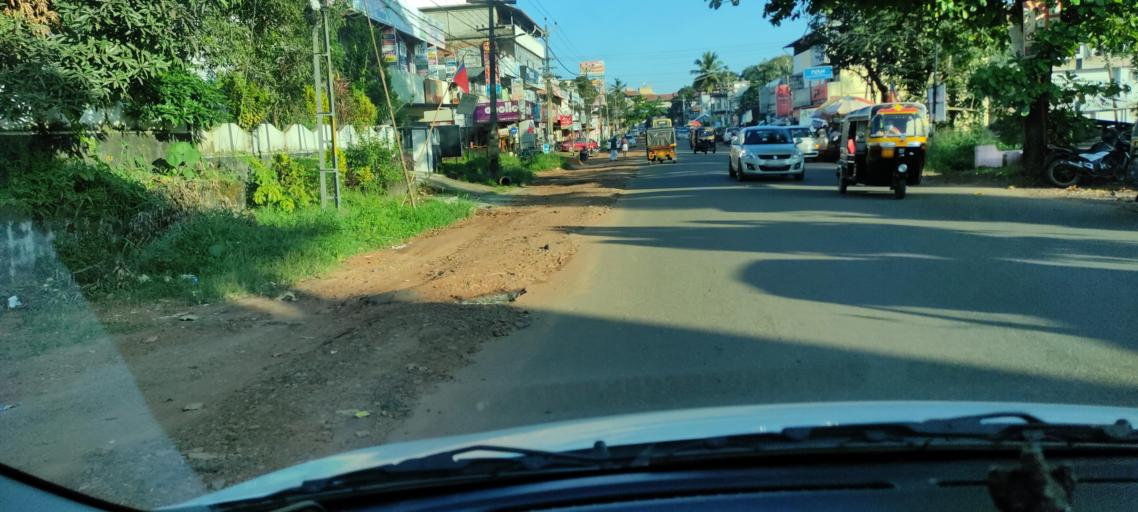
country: IN
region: Kerala
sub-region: Pattanamtitta
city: Adur
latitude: 9.1583
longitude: 76.7260
